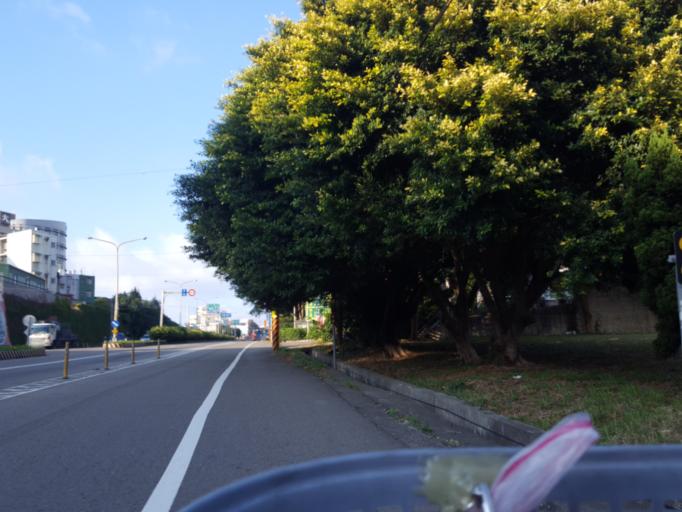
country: TW
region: Taiwan
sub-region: Hsinchu
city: Zhubei
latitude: 24.8610
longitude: 120.9915
